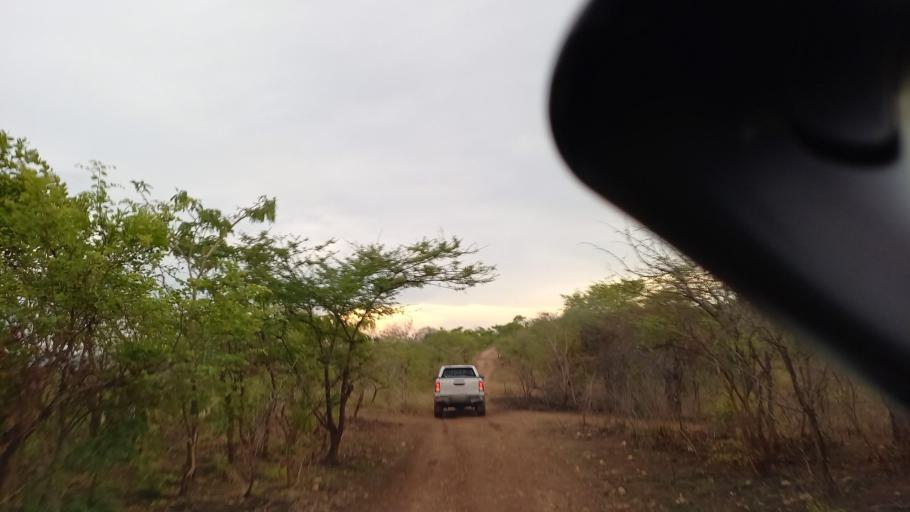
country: ZM
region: Lusaka
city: Kafue
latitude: -16.0468
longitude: 28.3173
